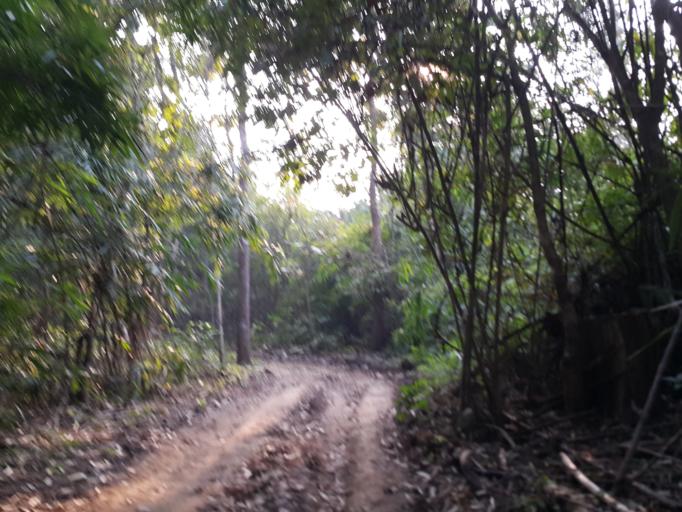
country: TH
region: Lamphun
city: Li
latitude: 17.6219
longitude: 98.9077
